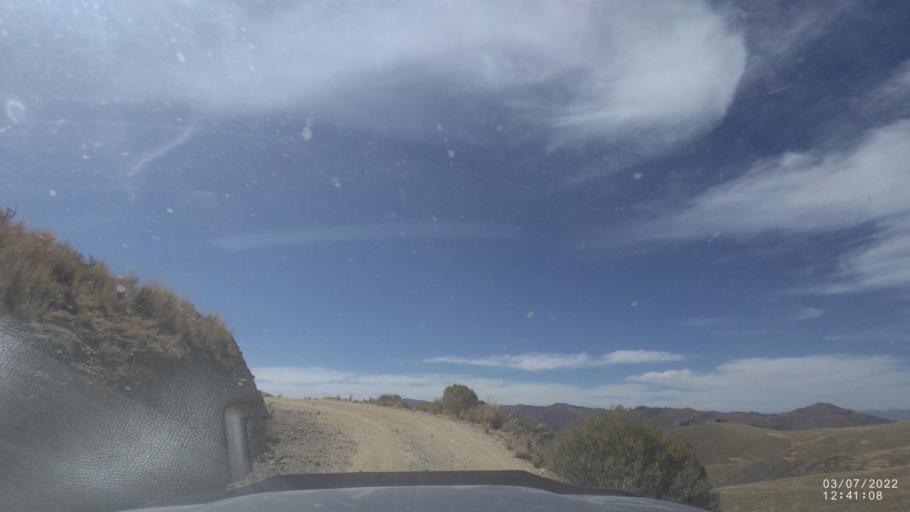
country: BO
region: Cochabamba
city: Irpa Irpa
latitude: -17.7873
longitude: -66.6243
